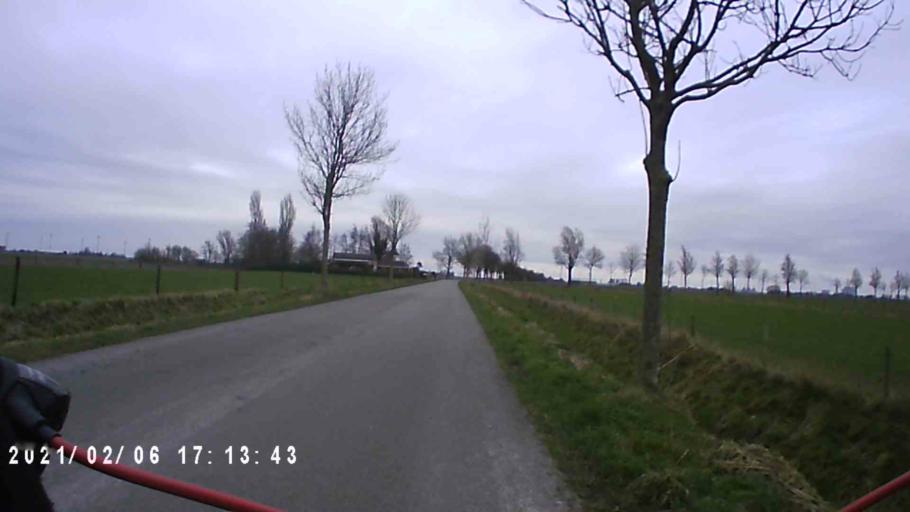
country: NL
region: Groningen
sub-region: Gemeente Appingedam
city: Appingedam
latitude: 53.4233
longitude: 6.7740
